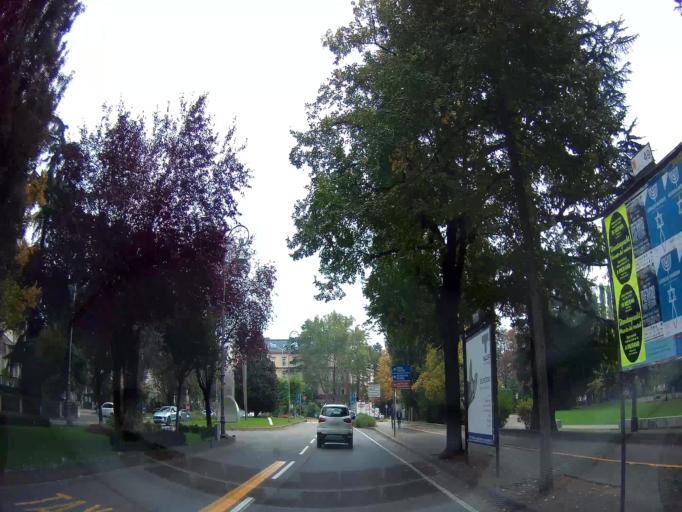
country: IT
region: Trentino-Alto Adige
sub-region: Bolzano
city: Merano
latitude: 46.6718
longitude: 11.1515
